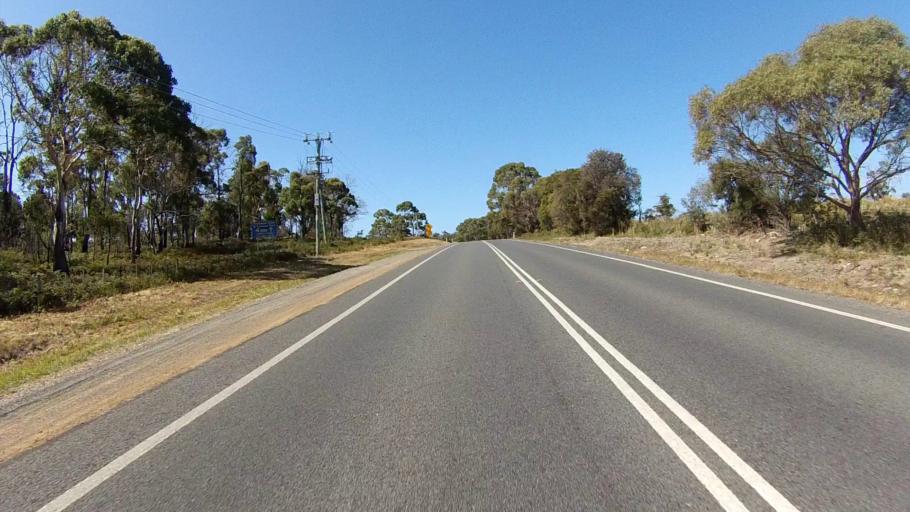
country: AU
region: Tasmania
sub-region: Sorell
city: Sorell
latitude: -42.5403
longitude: 147.8940
